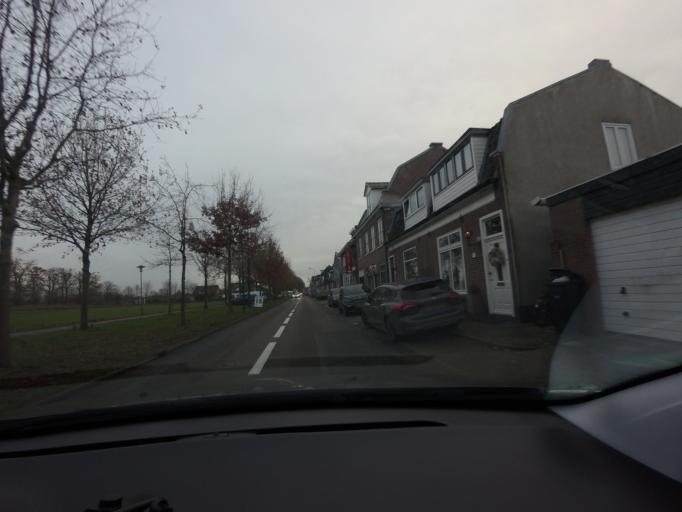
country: NL
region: North Holland
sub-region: Gemeente Wijdemeren
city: Kortenhoef
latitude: 52.2296
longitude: 5.1221
